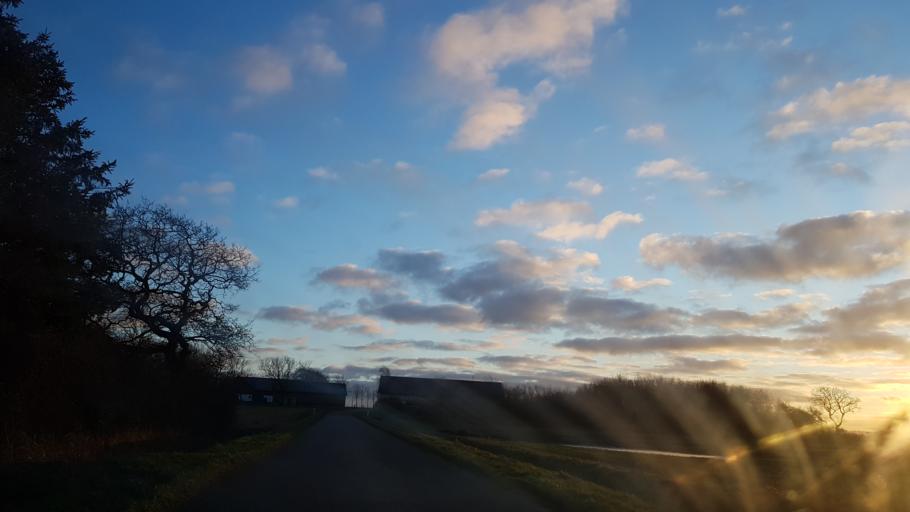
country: DK
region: South Denmark
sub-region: Kolding Kommune
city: Vamdrup
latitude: 55.3559
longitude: 9.2808
